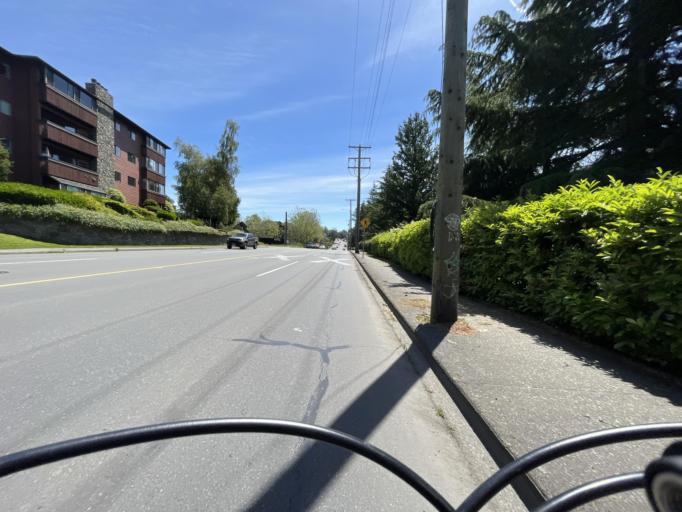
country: CA
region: British Columbia
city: Victoria
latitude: 48.4464
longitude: -123.3946
